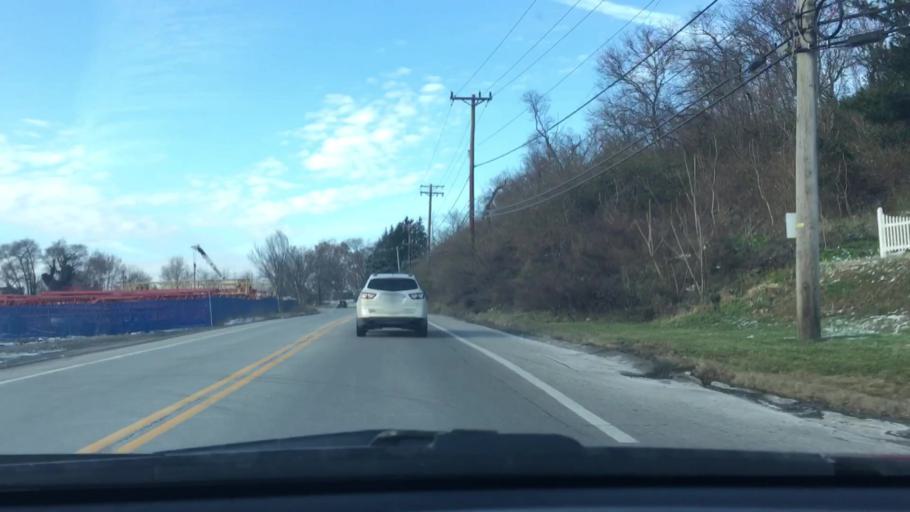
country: US
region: Pennsylvania
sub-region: Allegheny County
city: Glassport
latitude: 40.3408
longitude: -79.9152
